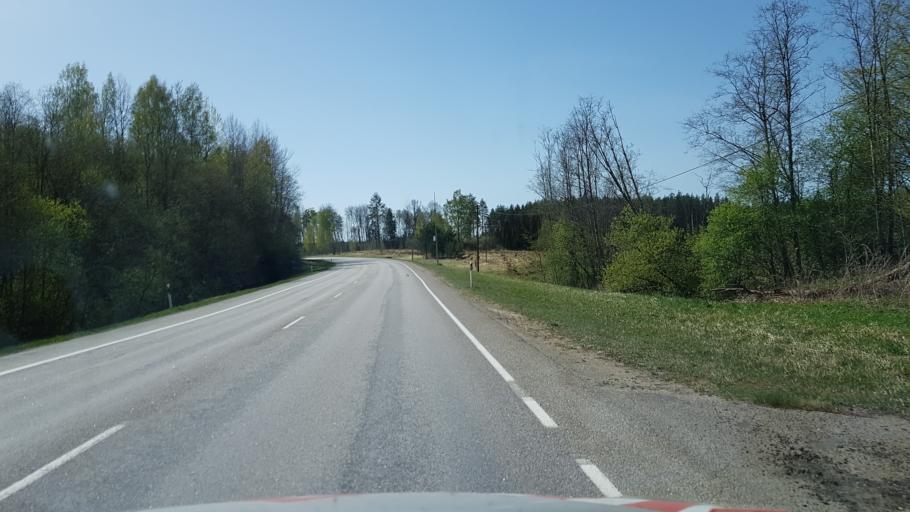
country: EE
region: Valgamaa
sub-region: Valga linn
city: Valga
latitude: 57.8674
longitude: 26.0578
